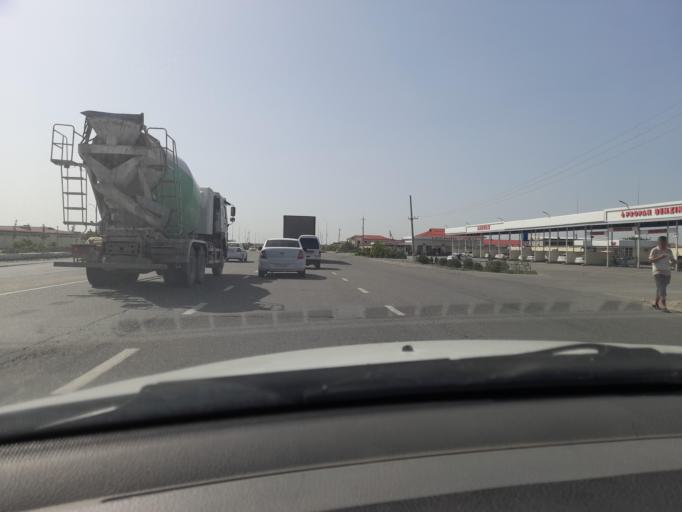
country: UZ
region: Samarqand
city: Daxbet
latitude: 39.7282
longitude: 66.9437
